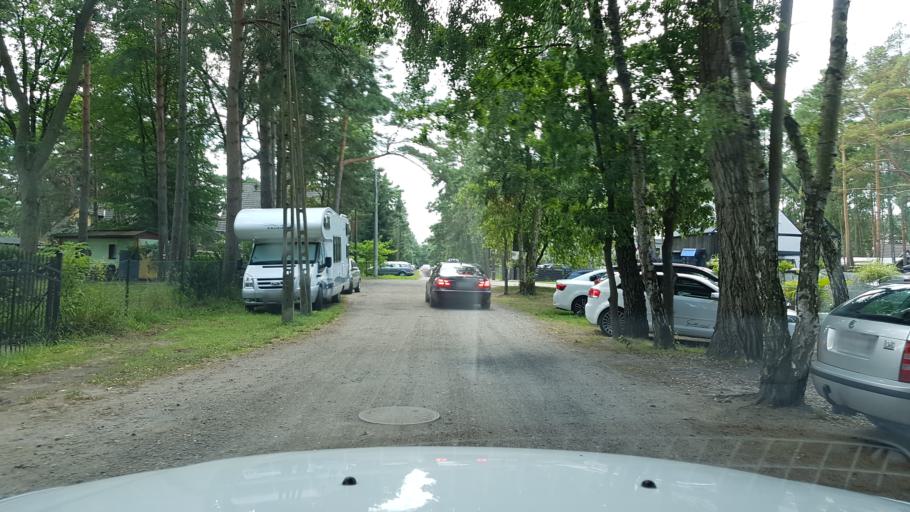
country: PL
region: West Pomeranian Voivodeship
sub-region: Powiat gryficki
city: Pobierowo
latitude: 54.0622
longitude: 14.9445
